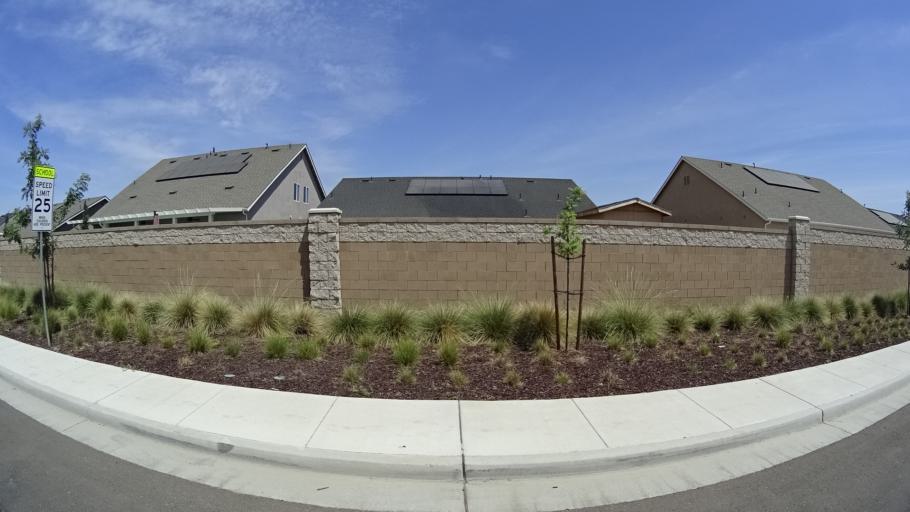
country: US
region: California
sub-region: Kings County
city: Armona
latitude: 36.3456
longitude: -119.6842
